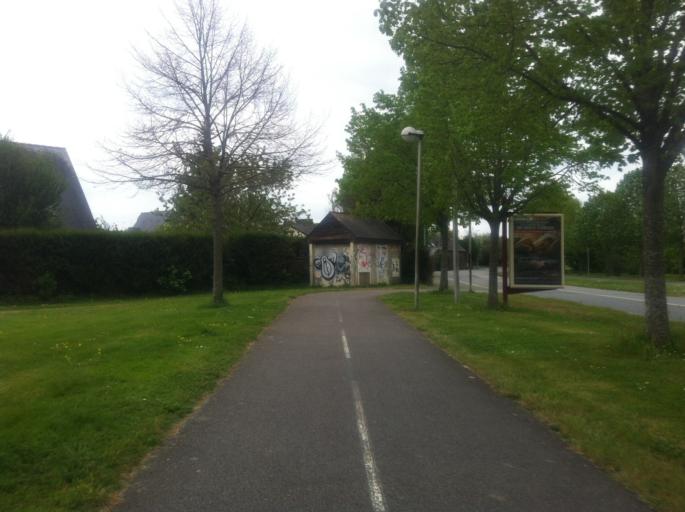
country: FR
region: Brittany
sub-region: Departement d'Ille-et-Vilaine
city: Bruz
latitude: 48.0261
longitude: -1.7324
